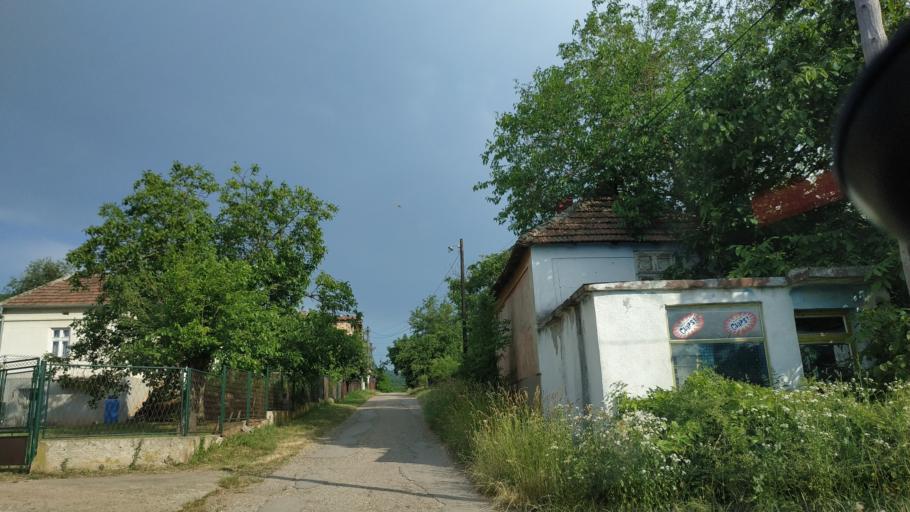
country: RS
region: Central Serbia
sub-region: Nisavski Okrug
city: Aleksinac
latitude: 43.6042
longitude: 21.6938
